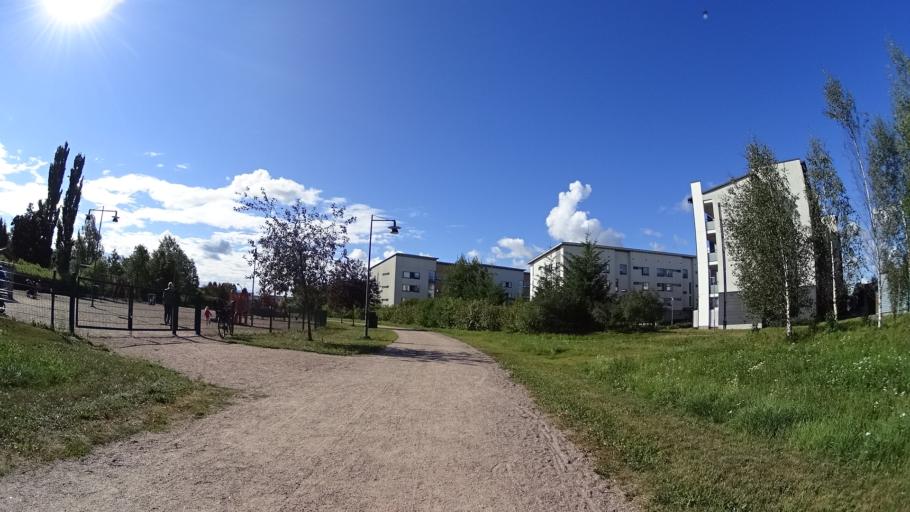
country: FI
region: Uusimaa
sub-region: Helsinki
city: Vantaa
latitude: 60.2737
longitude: 24.9647
